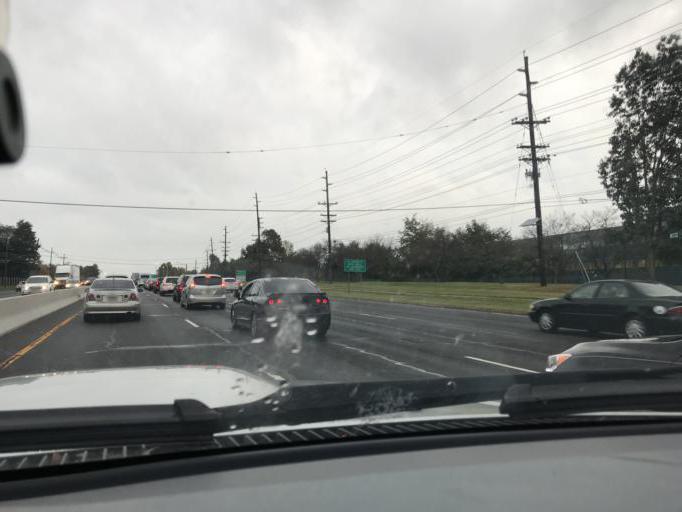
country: US
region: New Jersey
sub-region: Mercer County
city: Princeton
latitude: 40.3038
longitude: -74.6714
